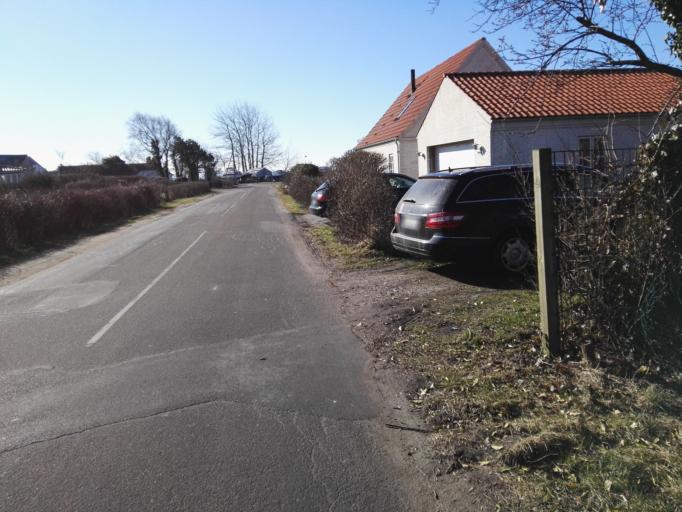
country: DK
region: Zealand
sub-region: Lejre Kommune
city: Ejby
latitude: 55.7581
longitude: 11.8030
